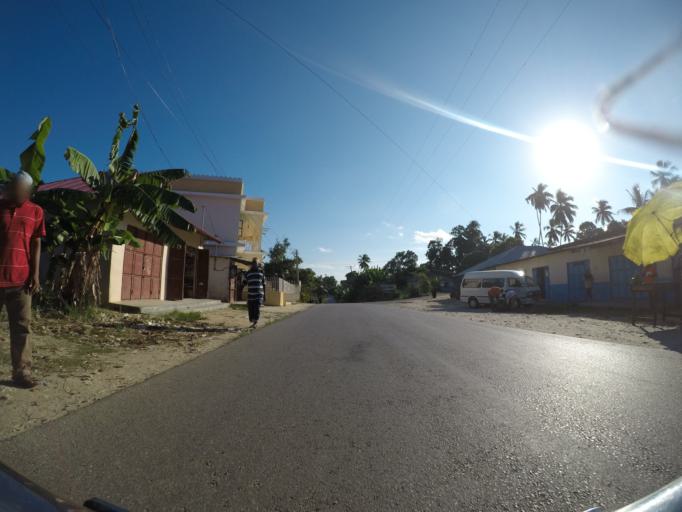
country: TZ
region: Pemba South
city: Chake Chake
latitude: -5.2925
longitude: 39.7603
